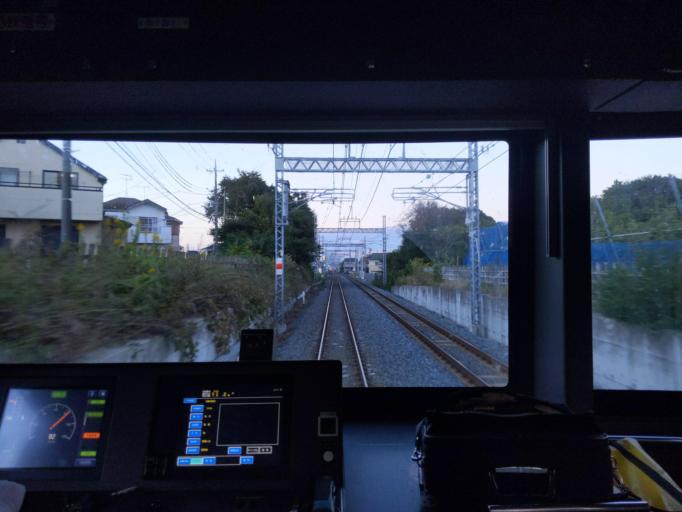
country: JP
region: Chiba
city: Kashiwa
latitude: 35.8005
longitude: 139.9991
